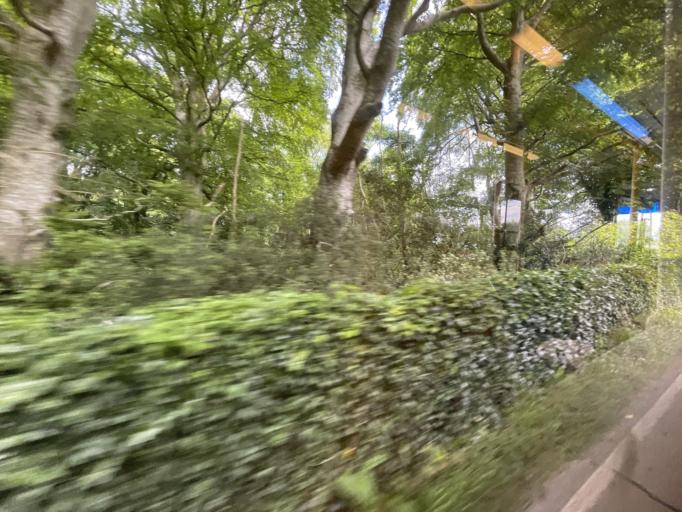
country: GB
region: Wales
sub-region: Anglesey
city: Beaumaris
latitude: 53.2661
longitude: -4.1130
